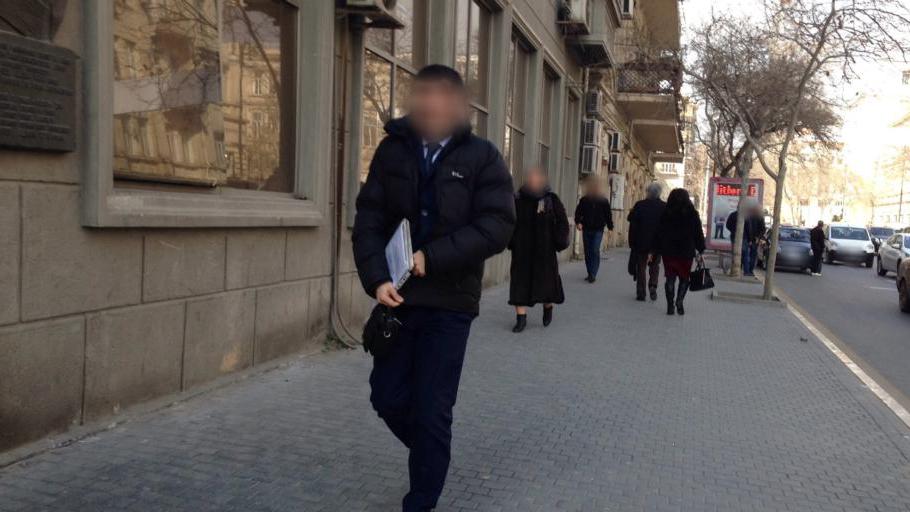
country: AZ
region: Baki
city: Baku
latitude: 40.3731
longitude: 49.8439
